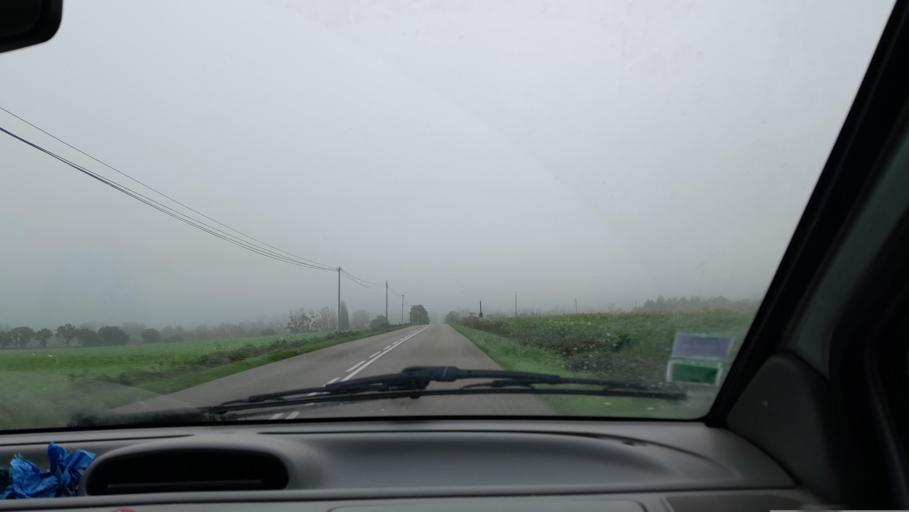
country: FR
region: Brittany
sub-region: Departement d'Ille-et-Vilaine
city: Le Pertre
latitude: 47.9921
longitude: -0.9860
